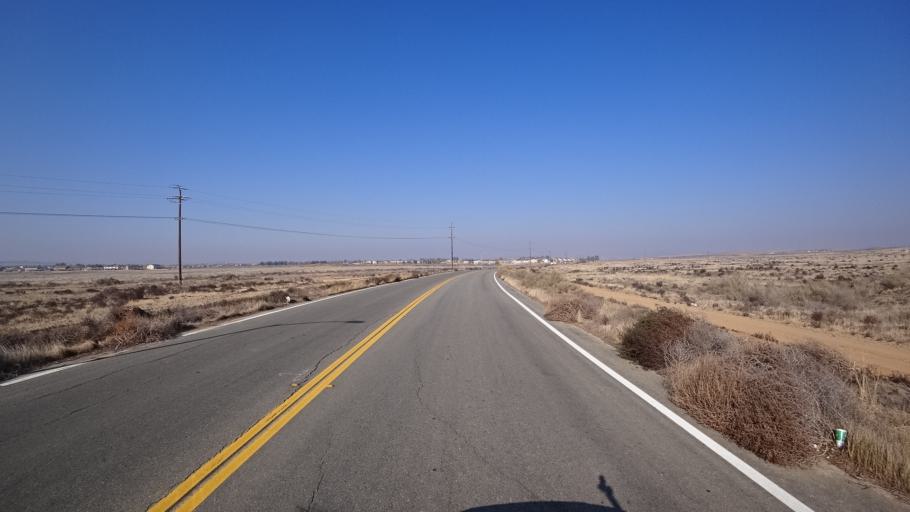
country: US
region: California
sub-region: Kern County
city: Oildale
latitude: 35.4015
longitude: -118.8781
